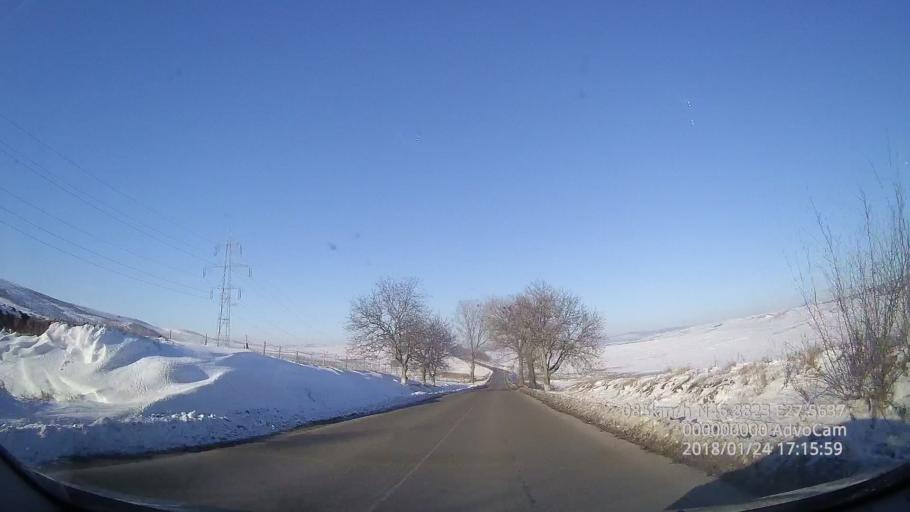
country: RO
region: Vaslui
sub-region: Comuna Rebricea
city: Rebricea
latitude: 46.8831
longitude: 27.5638
